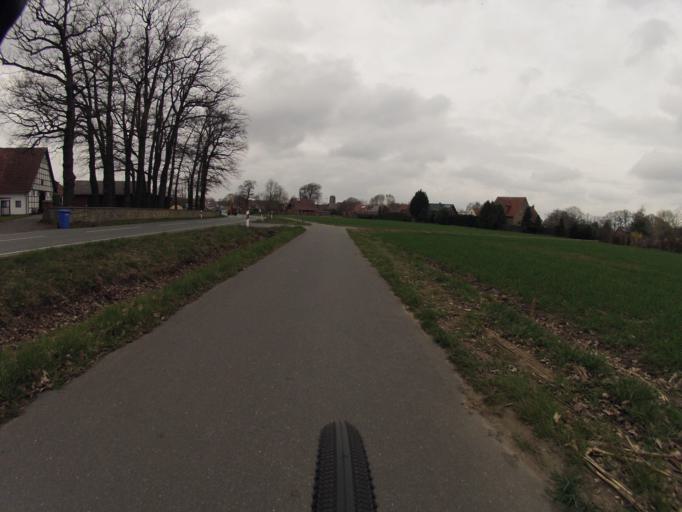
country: DE
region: North Rhine-Westphalia
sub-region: Regierungsbezirk Munster
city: Mettingen
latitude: 52.3293
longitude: 7.7553
